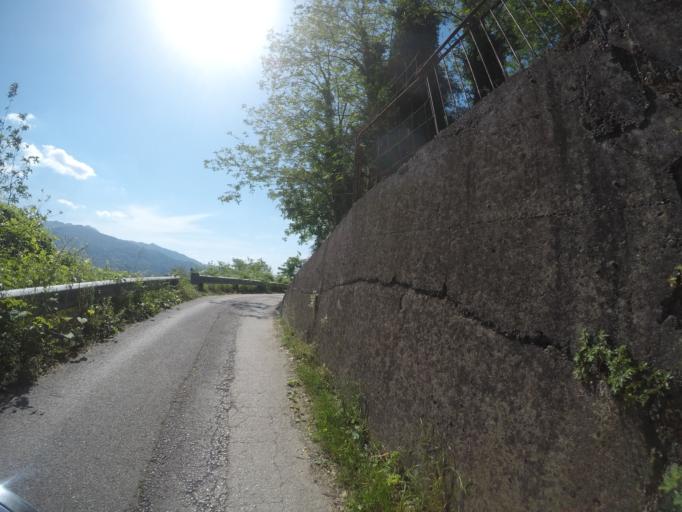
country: IT
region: Tuscany
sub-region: Provincia di Massa-Carrara
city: Massa
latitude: 44.0508
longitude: 10.1074
